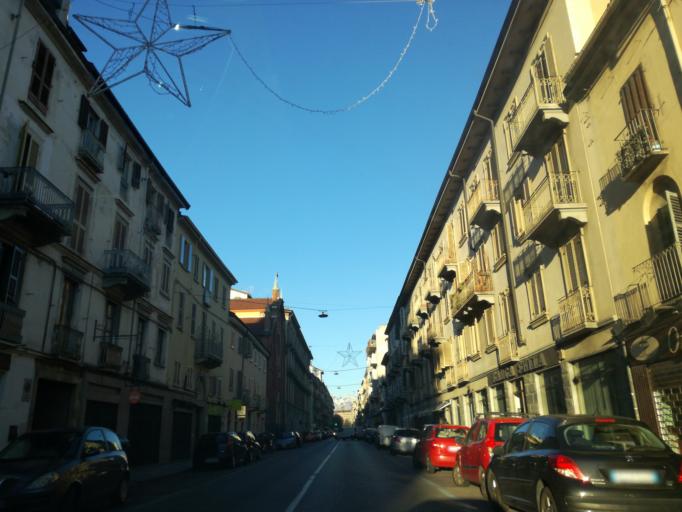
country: IT
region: Piedmont
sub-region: Provincia di Torino
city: Turin
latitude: 45.0798
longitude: 7.6656
